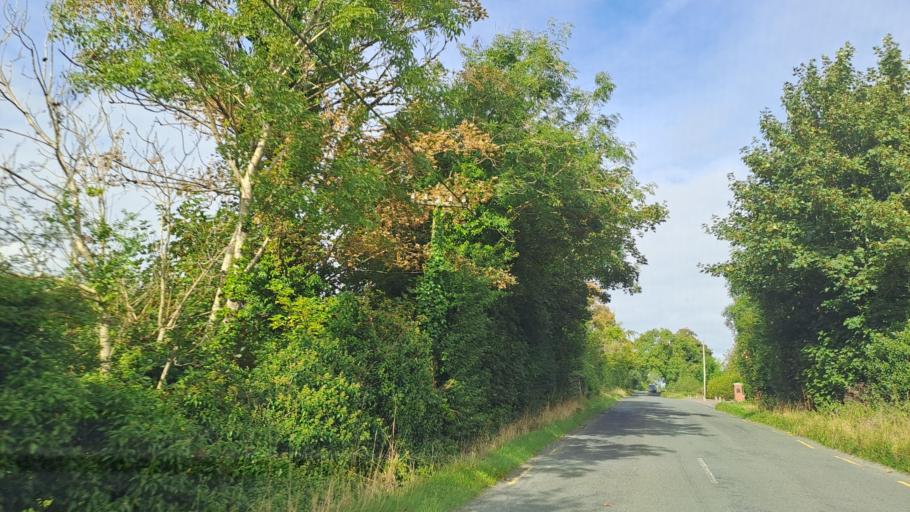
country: IE
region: Ulster
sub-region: An Cabhan
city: Kingscourt
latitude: 53.9628
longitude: -6.8558
